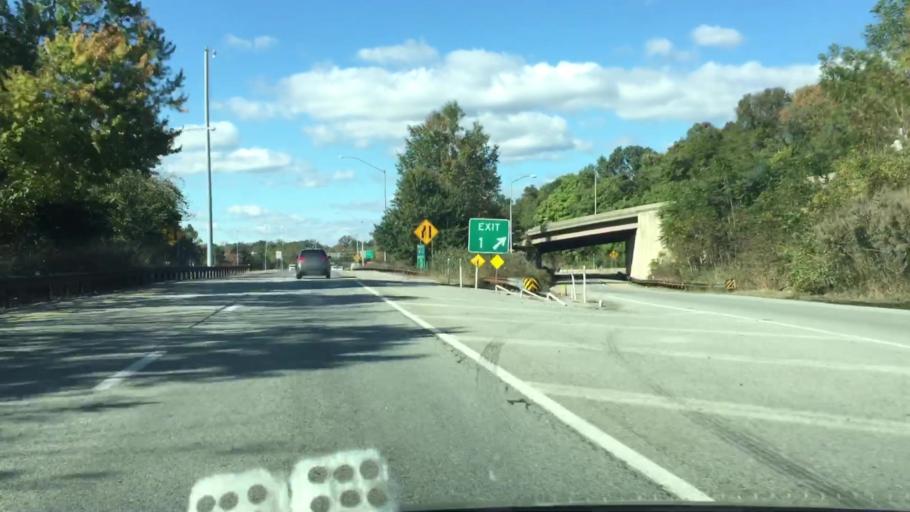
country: US
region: Pennsylvania
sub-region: Delaware County
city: Woodlyn
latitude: 39.8701
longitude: -75.3458
